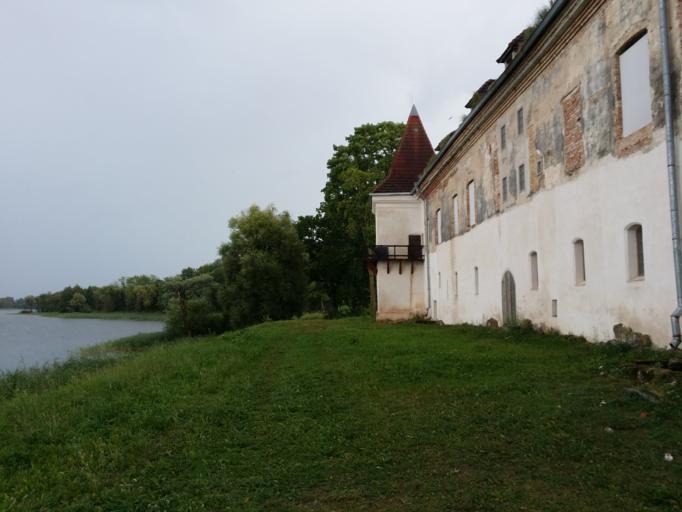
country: LT
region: Vilnius County
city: Ukmerge
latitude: 55.2867
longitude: 24.5135
